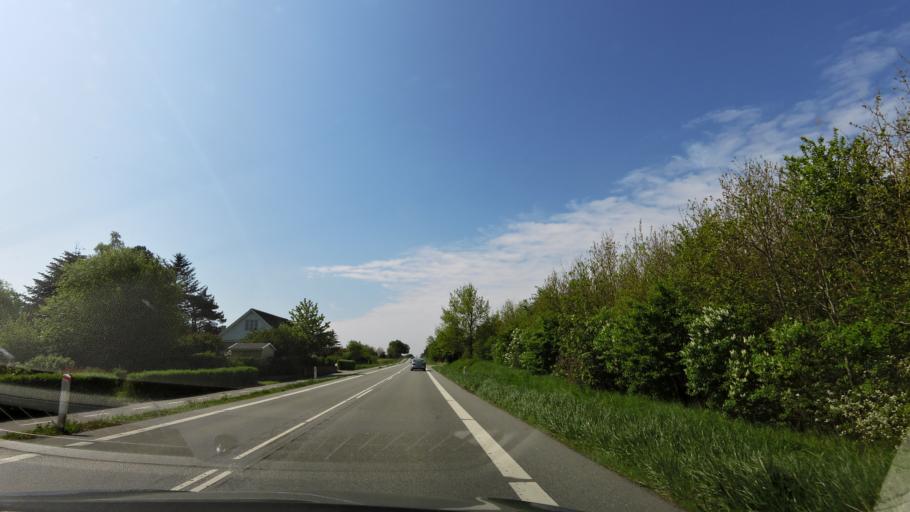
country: DK
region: South Denmark
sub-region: Nyborg Kommune
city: Ullerslev
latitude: 55.2870
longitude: 10.6952
